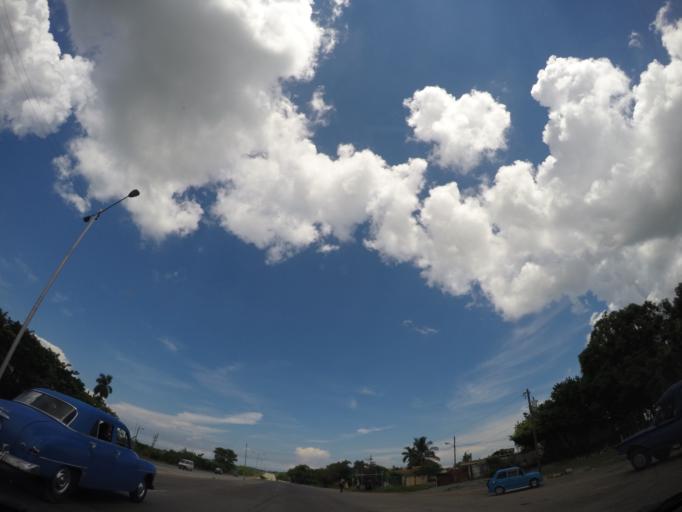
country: CU
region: La Habana
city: Havana
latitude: 23.1246
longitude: -82.4032
